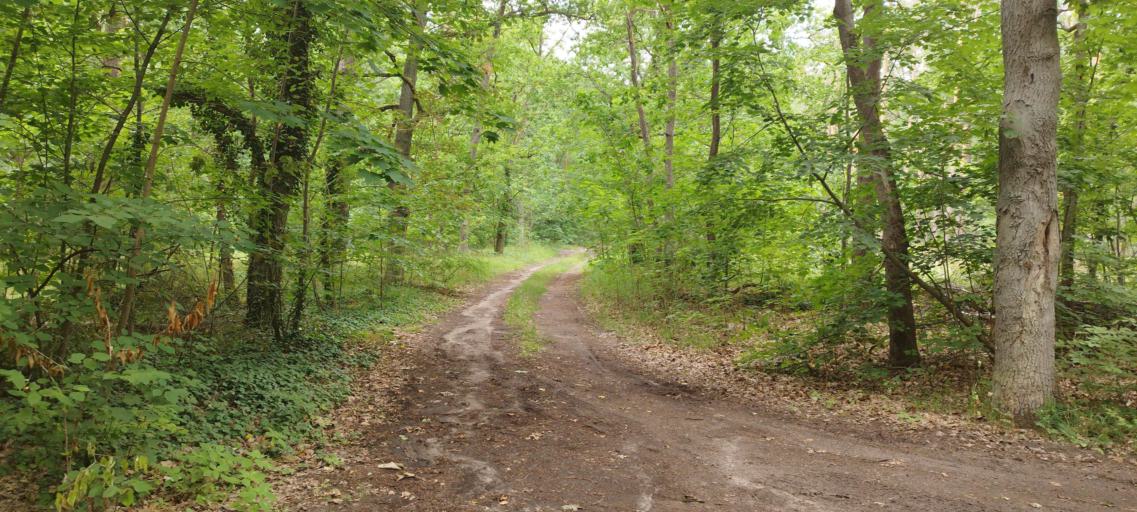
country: DE
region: Brandenburg
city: Woltersdorf
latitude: 52.4402
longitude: 13.7901
